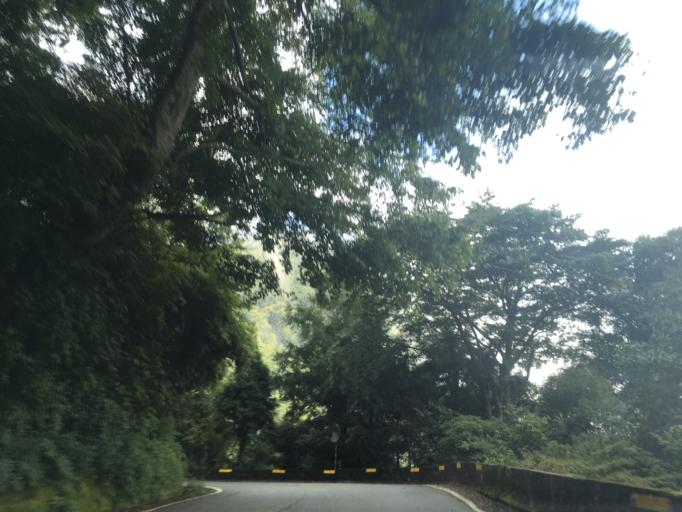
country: TW
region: Taiwan
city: Fengyuan
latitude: 24.2350
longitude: 120.9651
